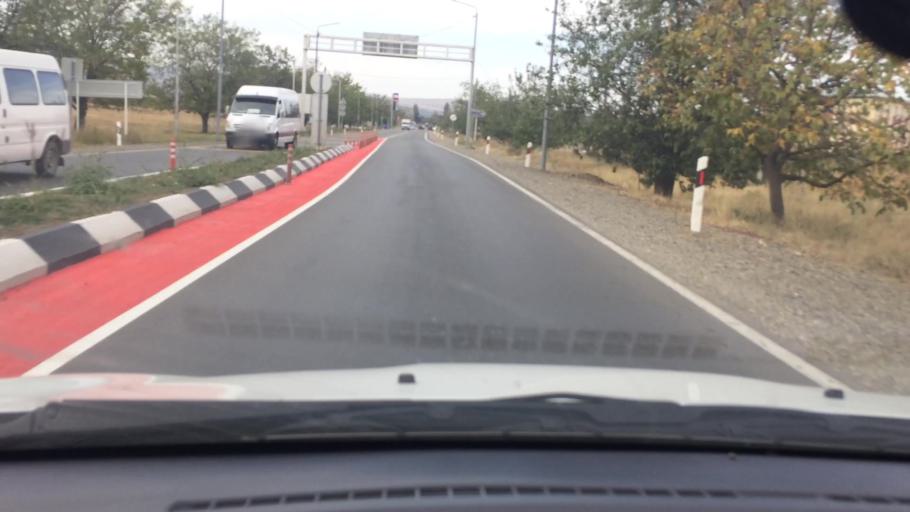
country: GE
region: Kvemo Kartli
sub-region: Marneuli
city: Marneuli
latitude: 41.5719
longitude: 44.7750
